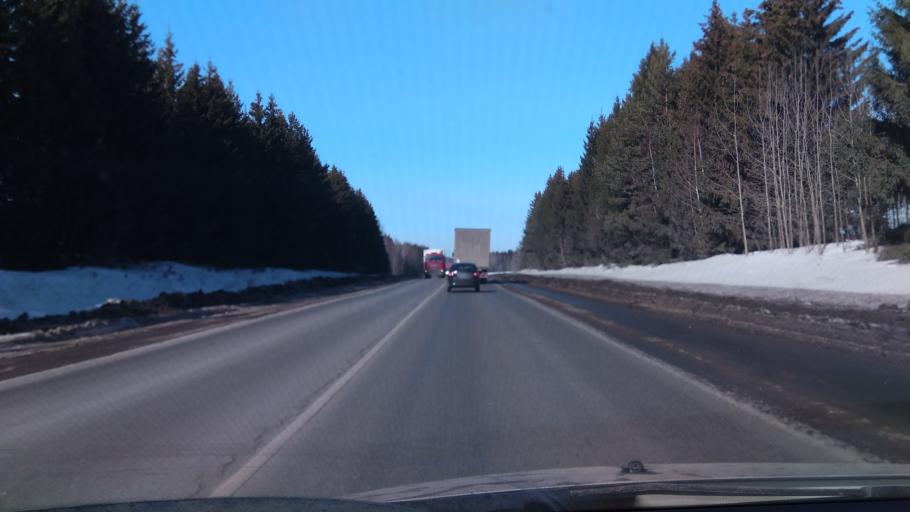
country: RU
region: Perm
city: Kukushtan
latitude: 57.5280
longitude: 56.6187
